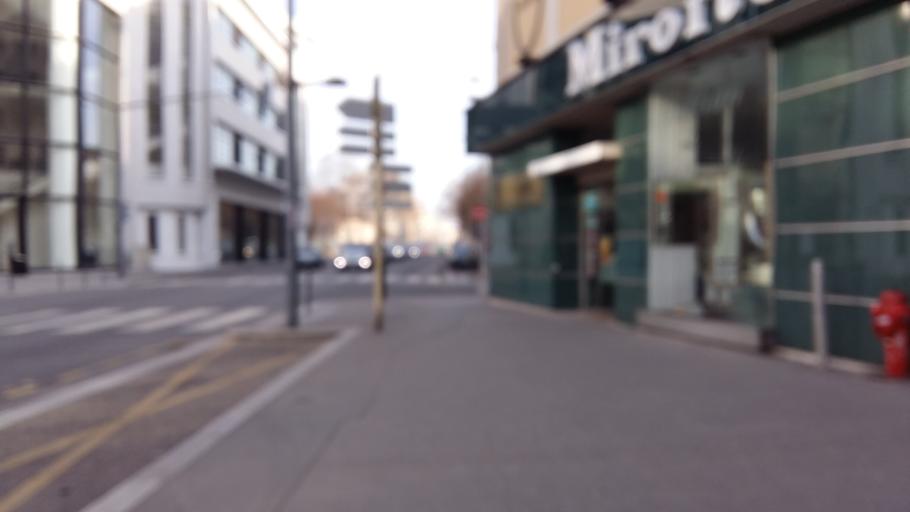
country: FR
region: Rhone-Alpes
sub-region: Departement du Rhone
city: Lyon
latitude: 45.7508
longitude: 4.8392
